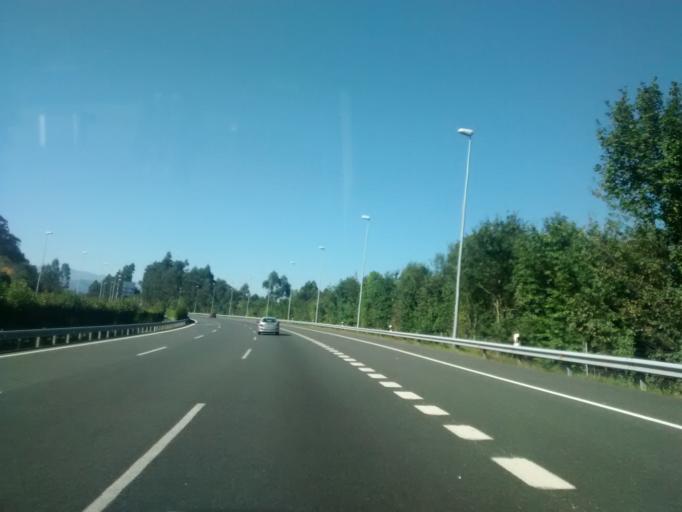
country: ES
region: Cantabria
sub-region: Provincia de Cantabria
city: Reocin
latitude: 43.3450
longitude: -4.1394
